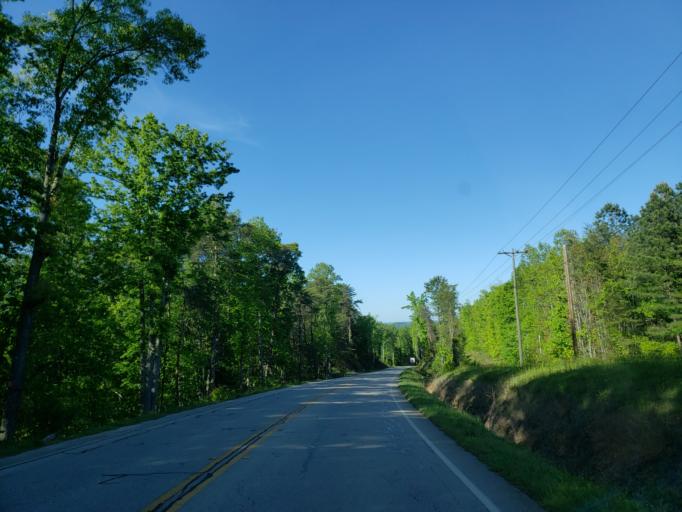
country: US
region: Georgia
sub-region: Polk County
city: Cedartown
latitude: 33.9052
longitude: -85.3126
